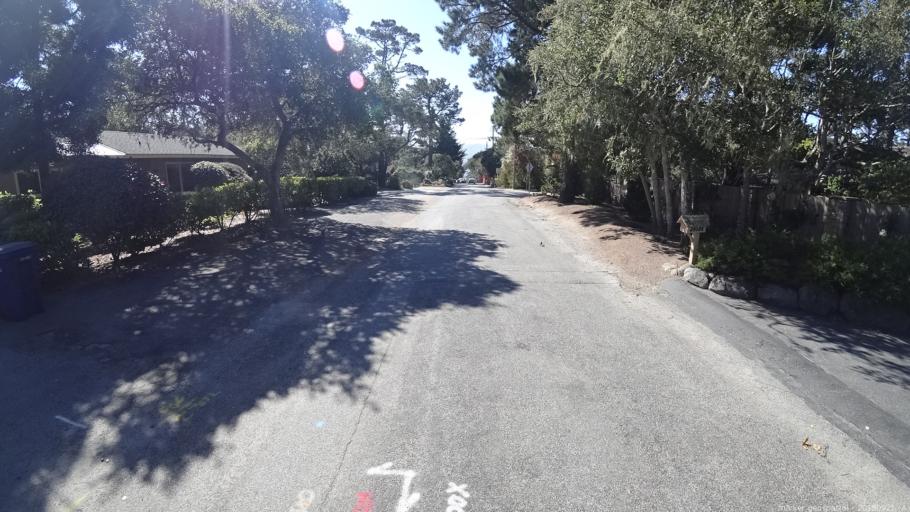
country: US
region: California
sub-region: Monterey County
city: Carmel-by-the-Sea
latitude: 36.5598
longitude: -121.9129
